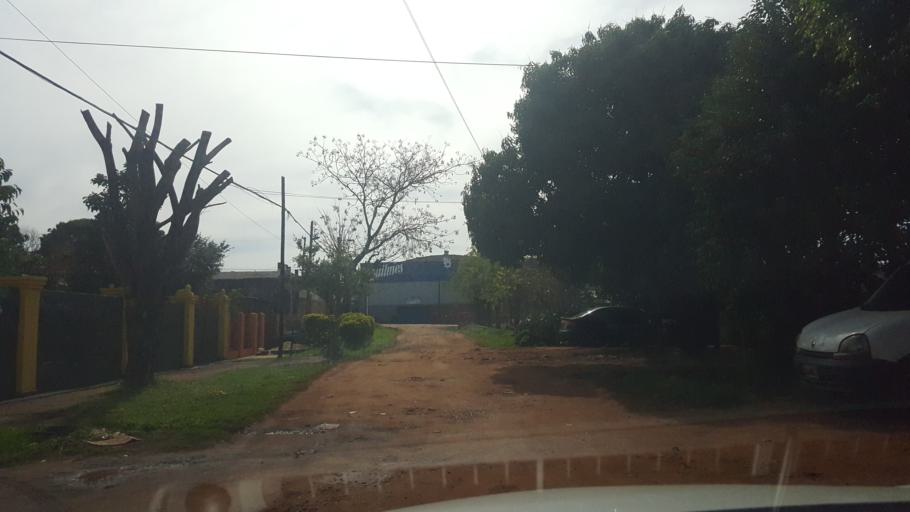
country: AR
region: Misiones
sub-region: Departamento de Capital
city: Posadas
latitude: -27.4105
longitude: -55.9102
